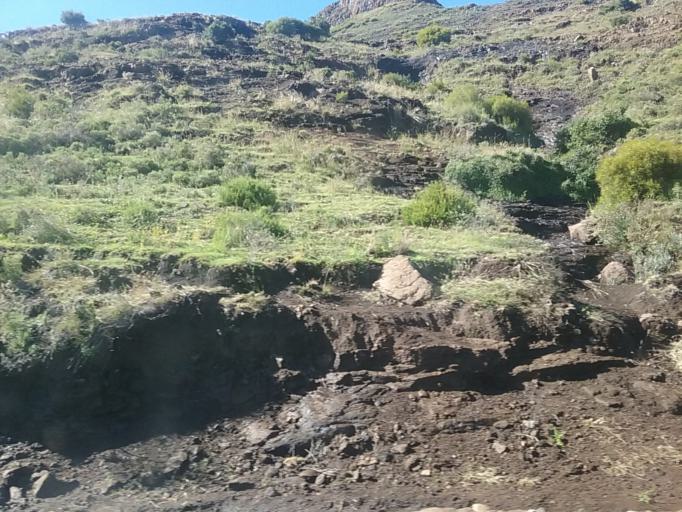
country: LS
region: Berea
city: Teyateyaneng
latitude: -29.2365
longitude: 27.9130
